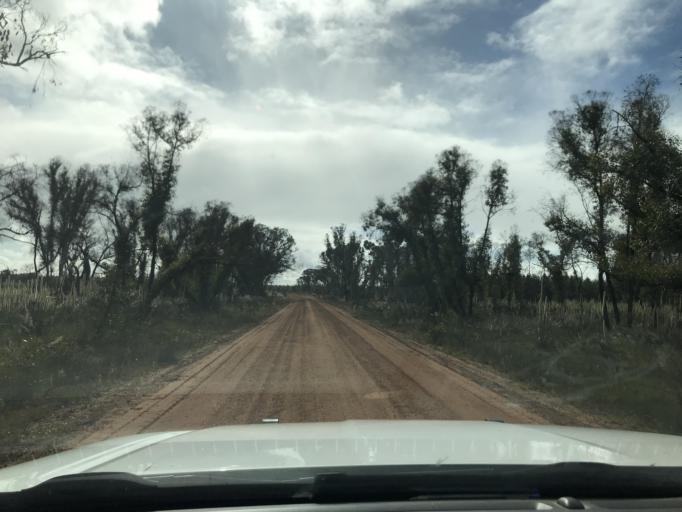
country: AU
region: South Australia
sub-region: Wattle Range
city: Penola
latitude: -37.1905
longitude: 141.1802
